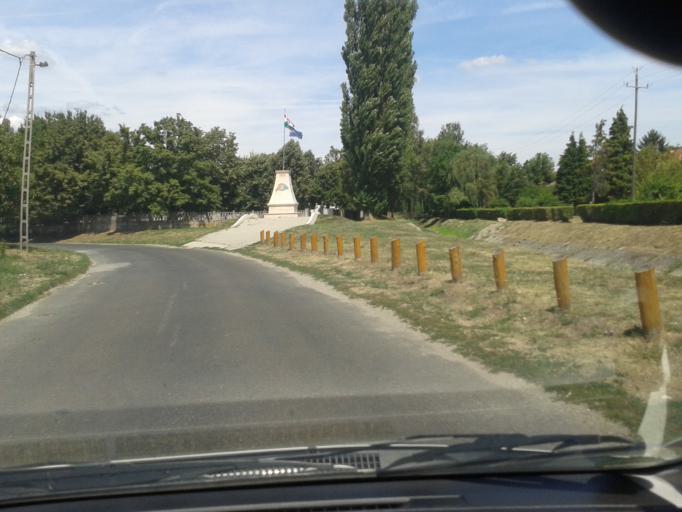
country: HU
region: Komarom-Esztergom
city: Pilismarot
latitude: 47.7855
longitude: 18.8754
